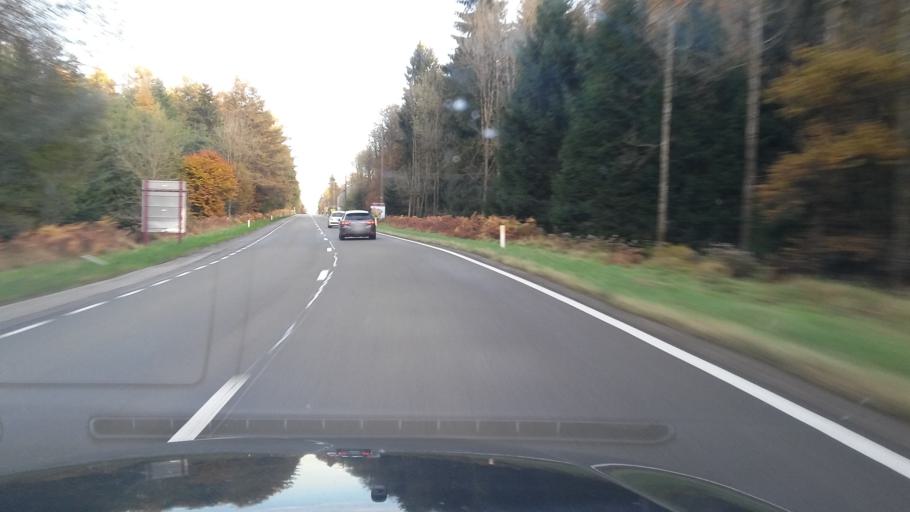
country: BE
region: Wallonia
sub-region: Province du Luxembourg
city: Bouillon
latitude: 49.7589
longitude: 5.1399
